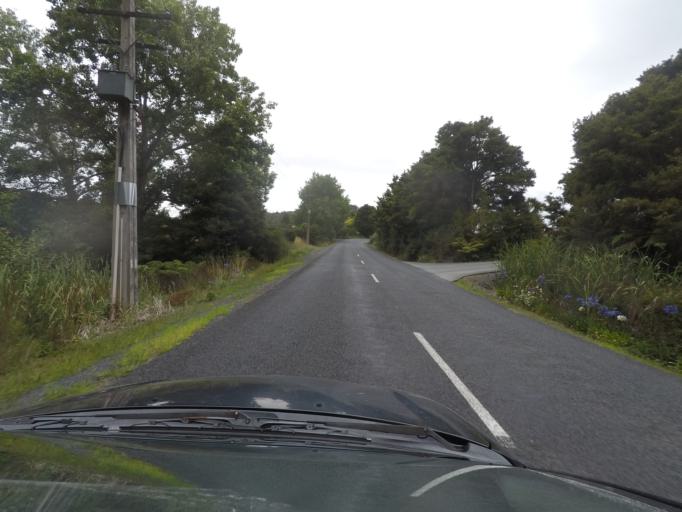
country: NZ
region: Auckland
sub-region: Auckland
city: Wellsford
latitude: -36.2790
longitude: 174.5857
